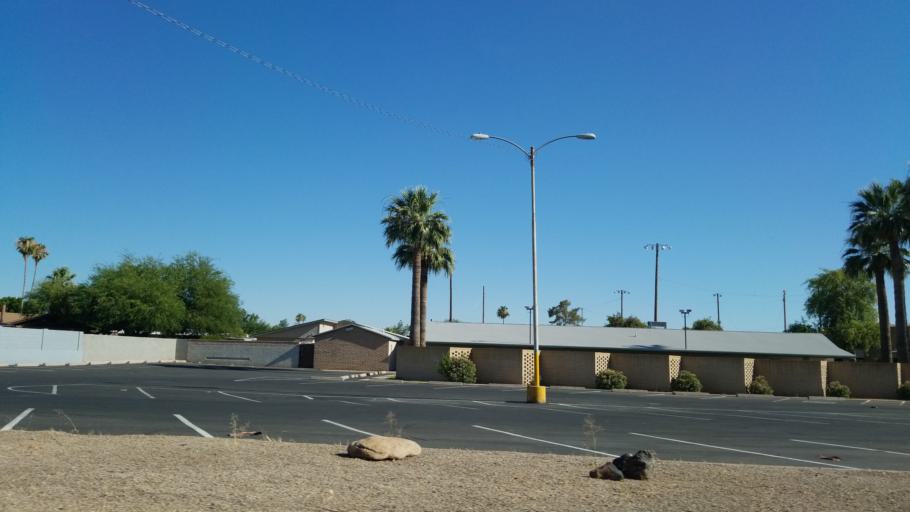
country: US
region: Arizona
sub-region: Maricopa County
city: Glendale
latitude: 33.5963
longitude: -112.1246
